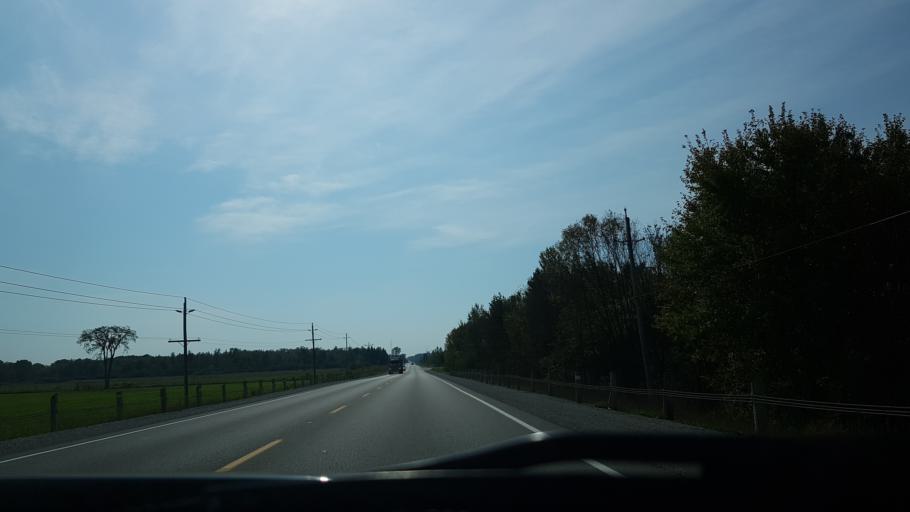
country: CA
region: Ontario
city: Orillia
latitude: 44.7130
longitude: -79.2813
